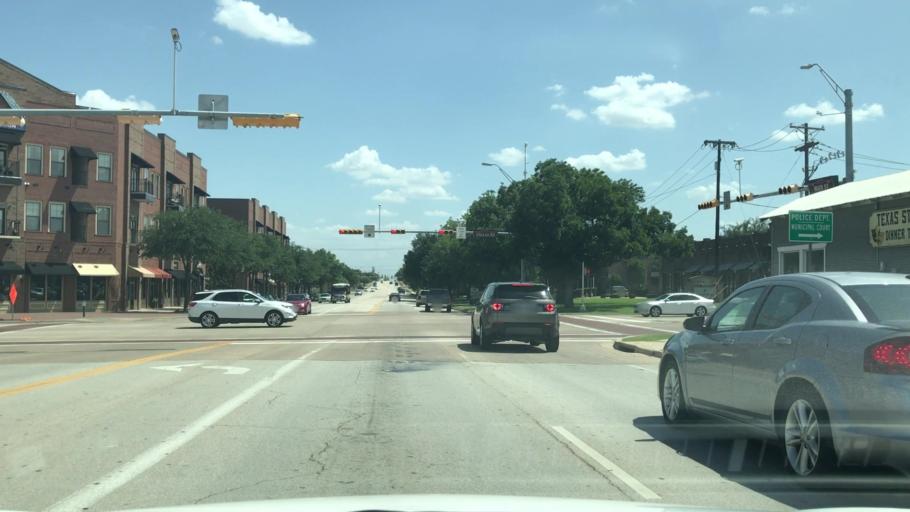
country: US
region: Texas
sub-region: Tarrant County
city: Grapevine
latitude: 32.9331
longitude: -97.0784
